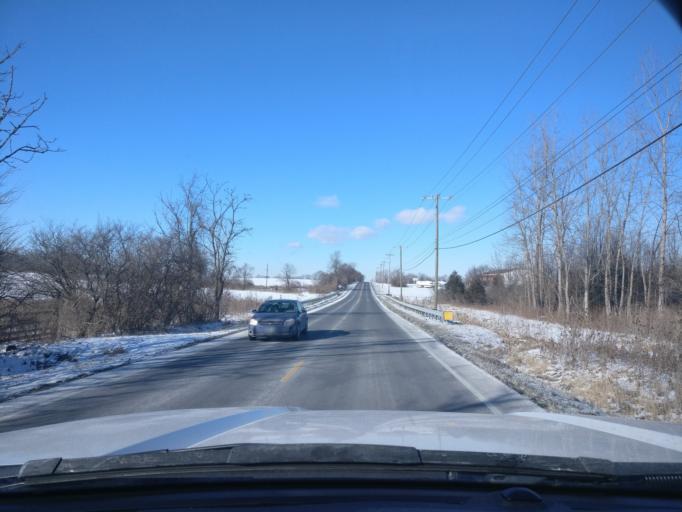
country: US
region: Ohio
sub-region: Warren County
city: Hunter
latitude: 39.5113
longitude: -84.2678
